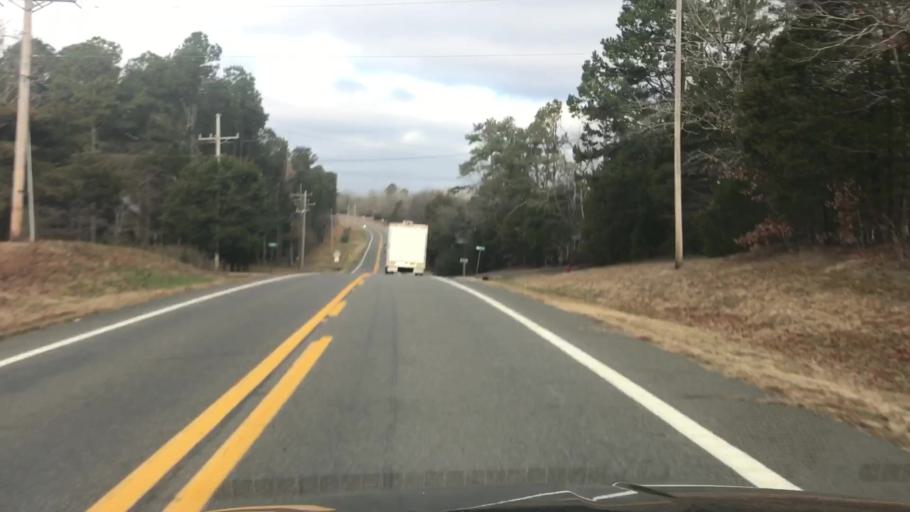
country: US
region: Arkansas
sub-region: Montgomery County
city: Mount Ida
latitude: 34.6214
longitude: -93.7236
